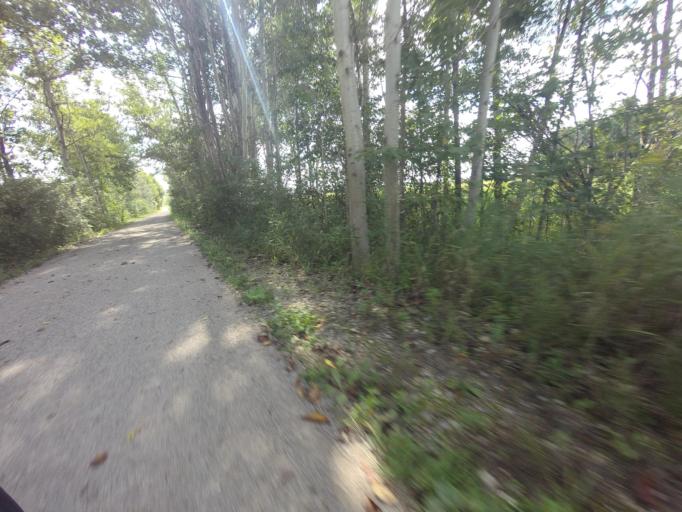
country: CA
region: Ontario
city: Huron East
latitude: 43.6978
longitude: -81.3423
